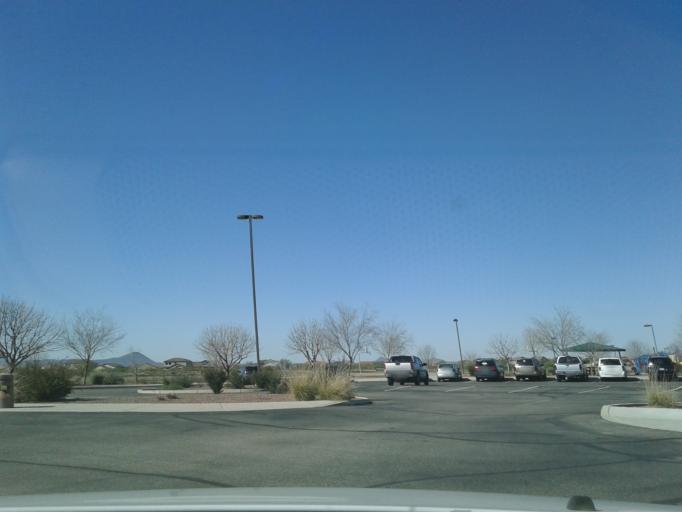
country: US
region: Arizona
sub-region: Pima County
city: Avra Valley
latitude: 32.5704
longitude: -111.3321
